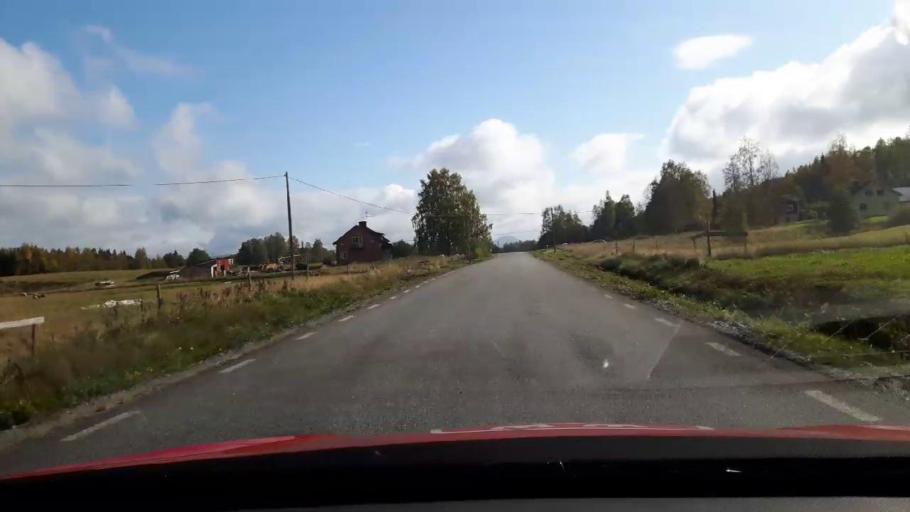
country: SE
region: Gaevleborg
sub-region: Ljusdals Kommun
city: Ljusdal
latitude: 61.7656
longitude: 16.0472
